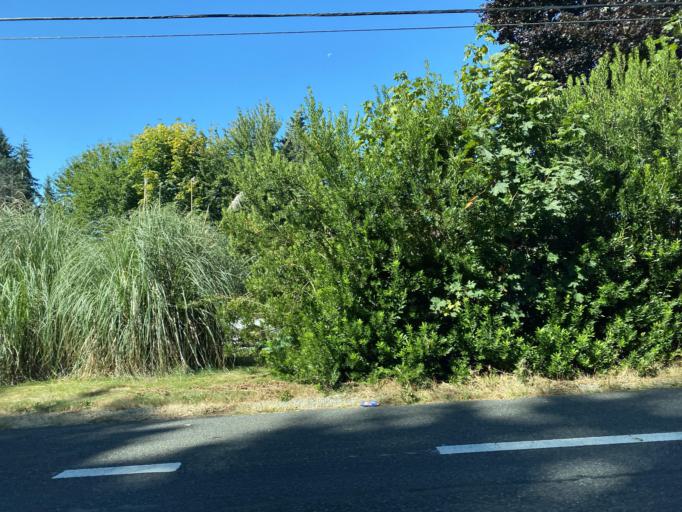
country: US
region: Washington
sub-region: Thurston County
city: Olympia
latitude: 47.0262
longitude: -122.8651
